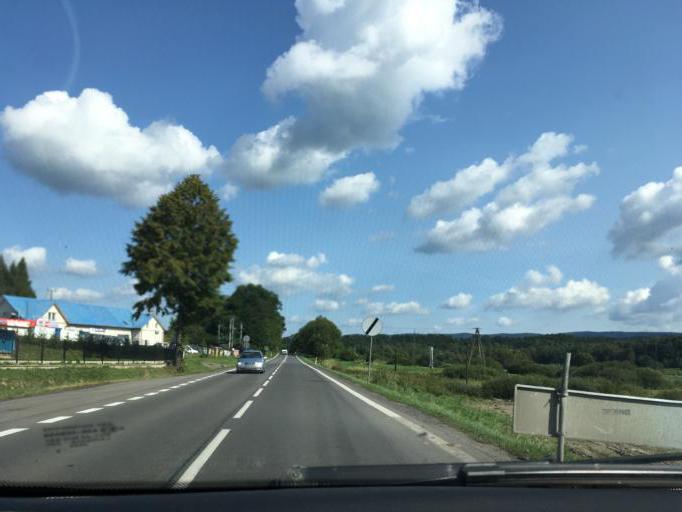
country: PL
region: Subcarpathian Voivodeship
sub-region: Powiat leski
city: Lesko
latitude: 49.4823
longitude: 22.3234
